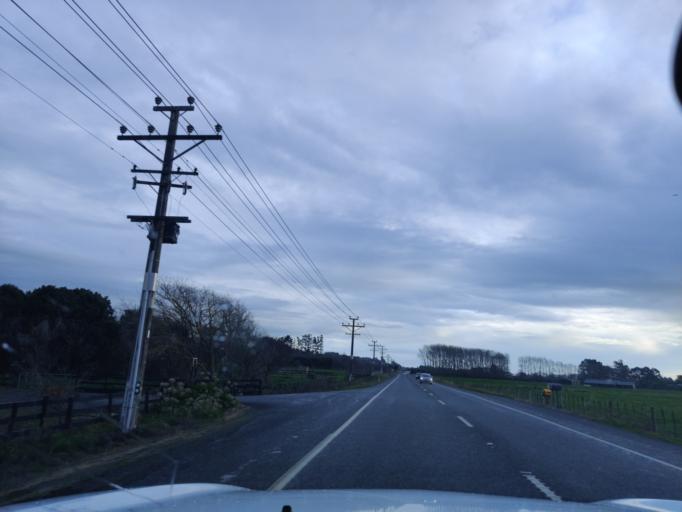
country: NZ
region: Manawatu-Wanganui
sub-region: Palmerston North City
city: Palmerston North
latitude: -40.3513
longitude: 175.6966
